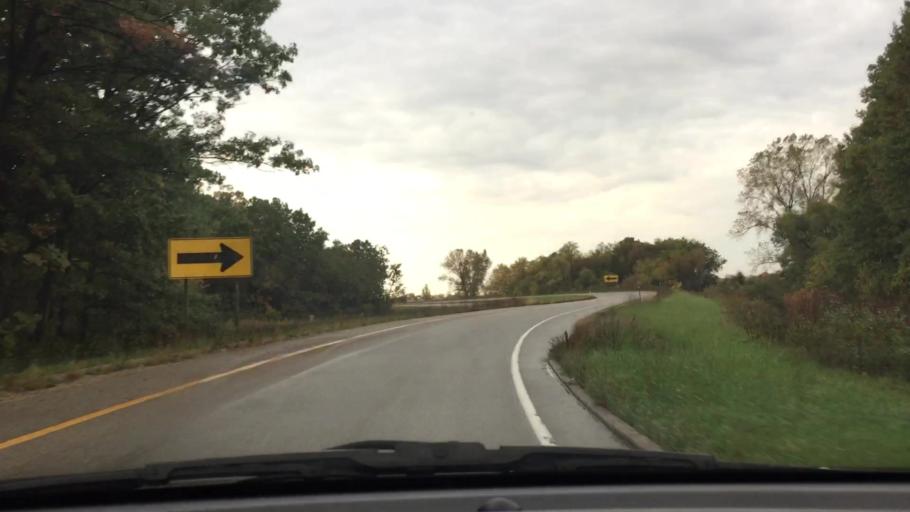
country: US
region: Wisconsin
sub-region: Walworth County
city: Elkhorn
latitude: 42.6757
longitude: -88.5236
